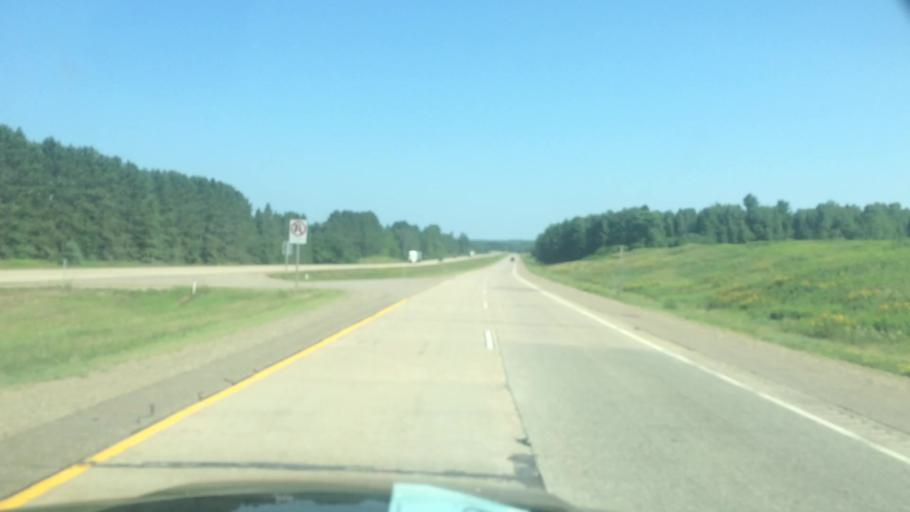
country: US
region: Wisconsin
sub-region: Lincoln County
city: Tomahawk
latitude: 45.3584
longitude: -89.6667
